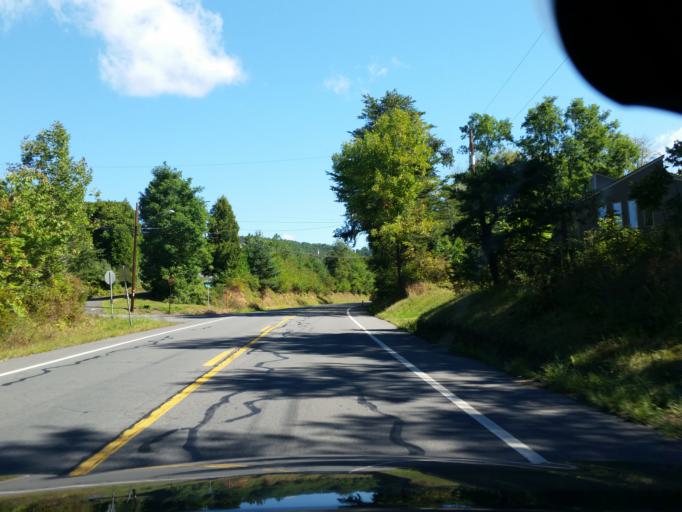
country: US
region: Pennsylvania
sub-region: Northumberland County
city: Elysburg
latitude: 40.8690
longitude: -76.5434
